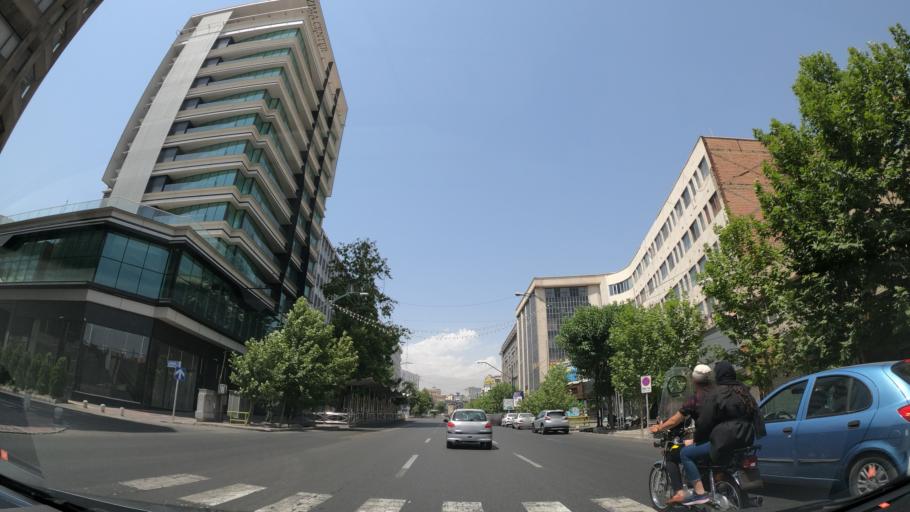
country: IR
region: Tehran
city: Tehran
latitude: 35.7264
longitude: 51.4142
